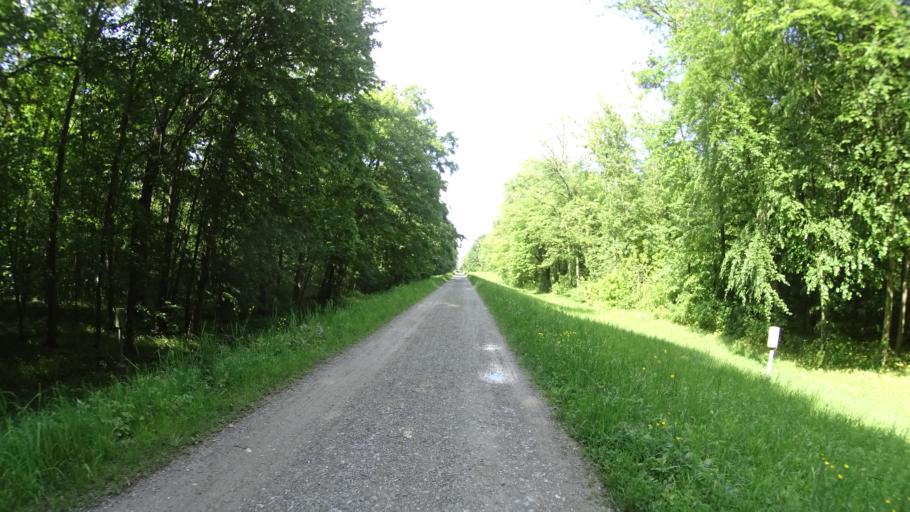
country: DE
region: Baden-Wuerttemberg
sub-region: Karlsruhe Region
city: Rheinstetten
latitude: 49.0043
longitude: 8.2974
